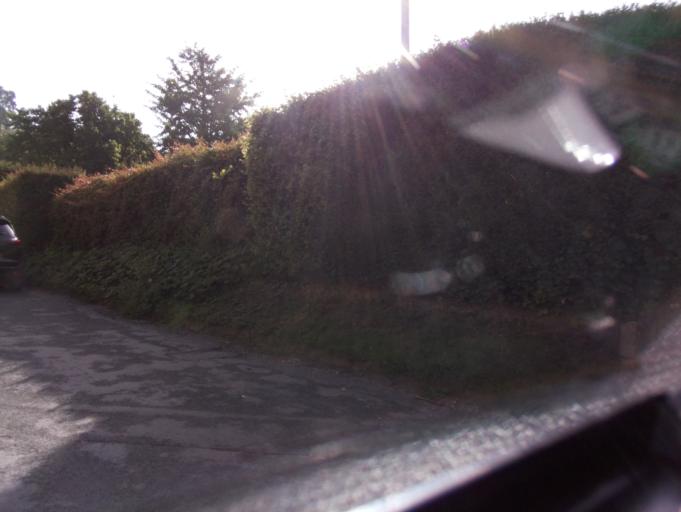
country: GB
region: England
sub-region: Oxfordshire
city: Shrivenham
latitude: 51.6404
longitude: -1.6603
